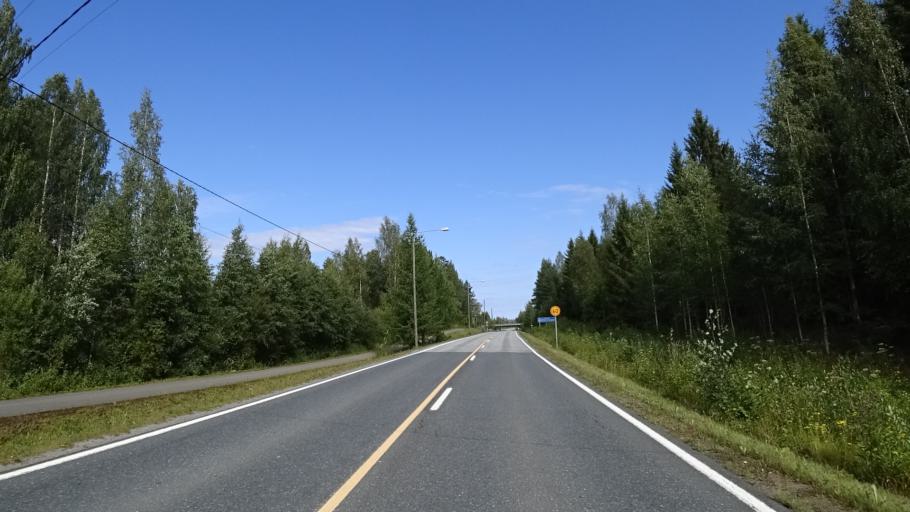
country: FI
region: North Karelia
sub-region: Joensuu
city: Pyhaeselkae
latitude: 62.4741
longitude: 29.9519
